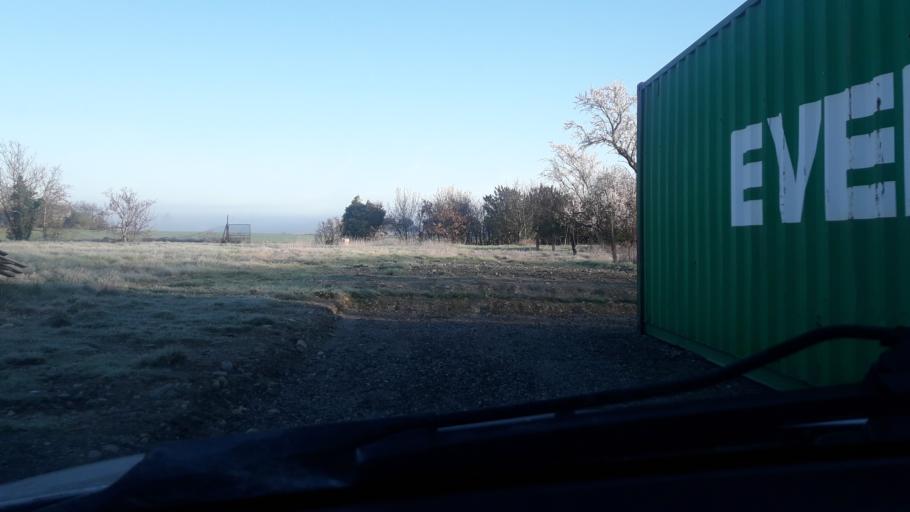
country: FR
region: Midi-Pyrenees
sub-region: Departement de la Haute-Garonne
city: Carbonne
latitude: 43.2968
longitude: 1.2094
